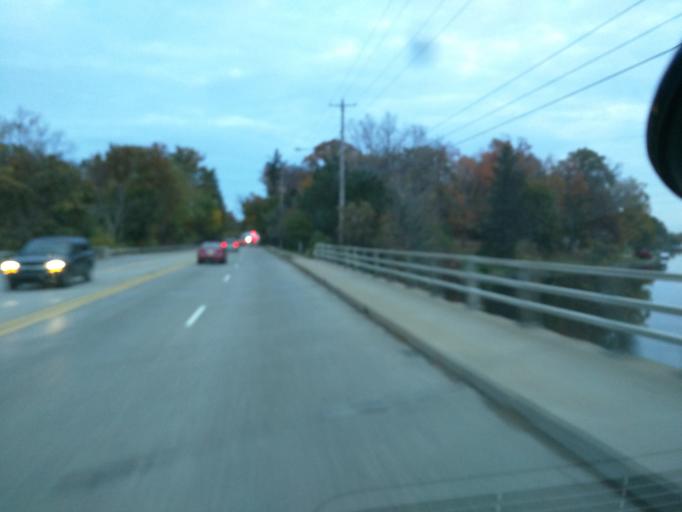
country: US
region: Michigan
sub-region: Eaton County
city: Waverly
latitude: 42.7094
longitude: -84.6030
